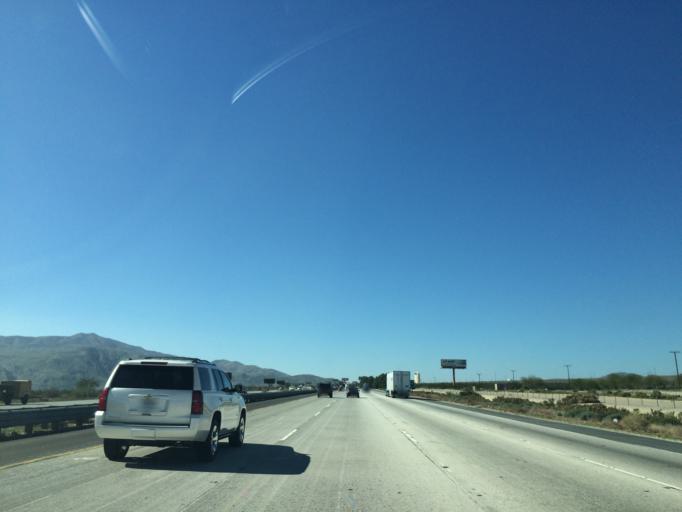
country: US
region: California
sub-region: Riverside County
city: Cabazon
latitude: 33.9211
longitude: -116.7537
